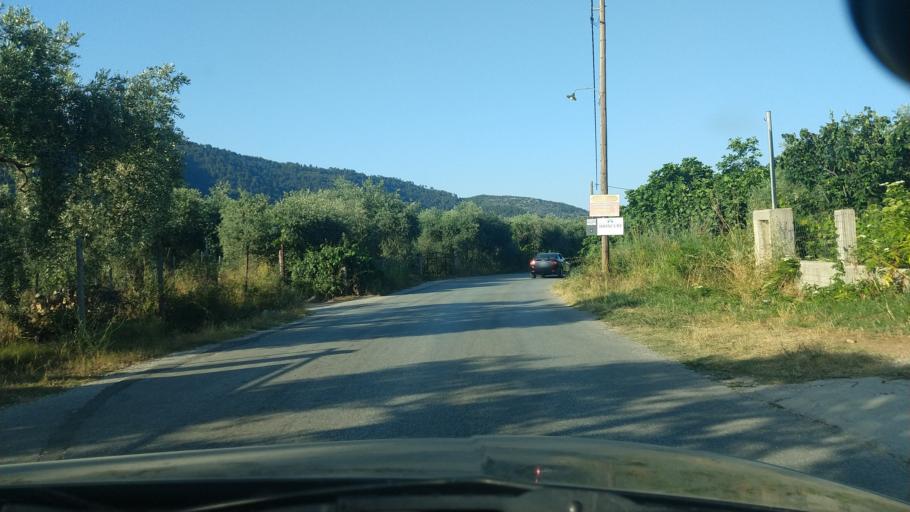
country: GR
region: East Macedonia and Thrace
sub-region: Nomos Kavalas
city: Potamia
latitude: 40.7176
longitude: 24.7474
